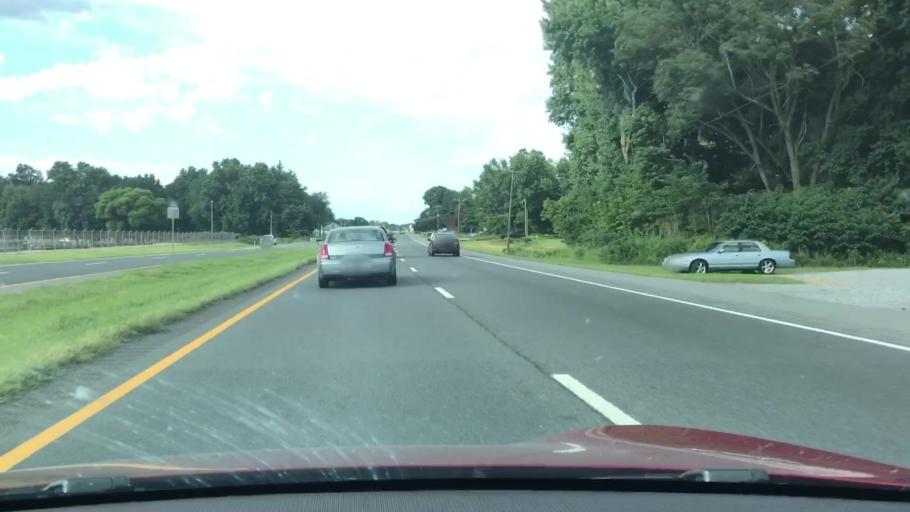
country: US
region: Delaware
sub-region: Sussex County
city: Bridgeville
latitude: 38.7914
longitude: -75.5894
